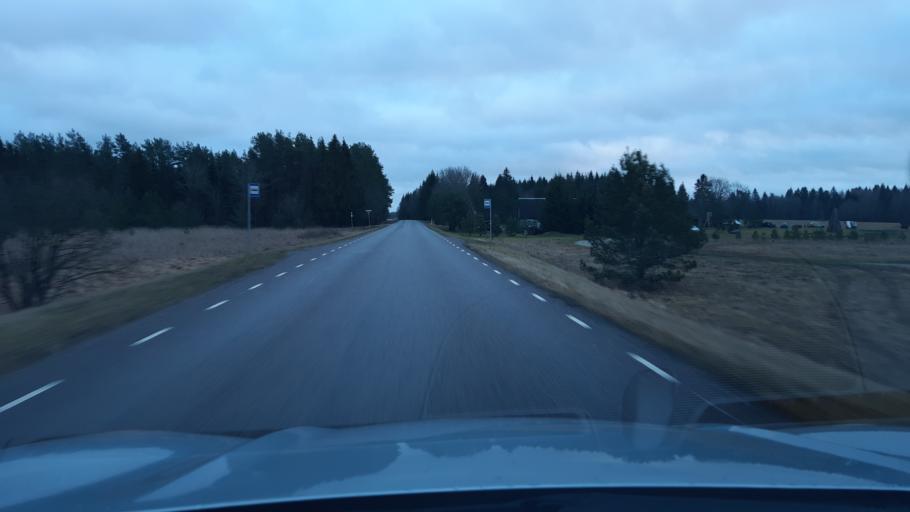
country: EE
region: Raplamaa
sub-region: Kohila vald
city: Kohila
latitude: 59.1282
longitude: 24.6688
